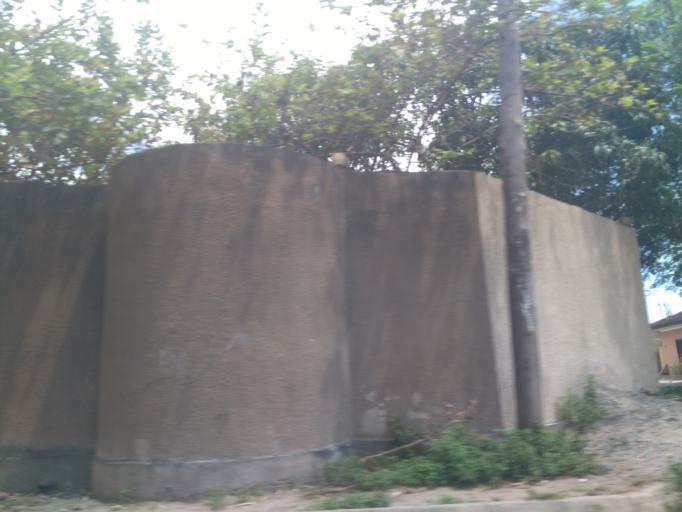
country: TZ
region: Dar es Salaam
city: Magomeni
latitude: -6.7935
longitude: 39.2700
